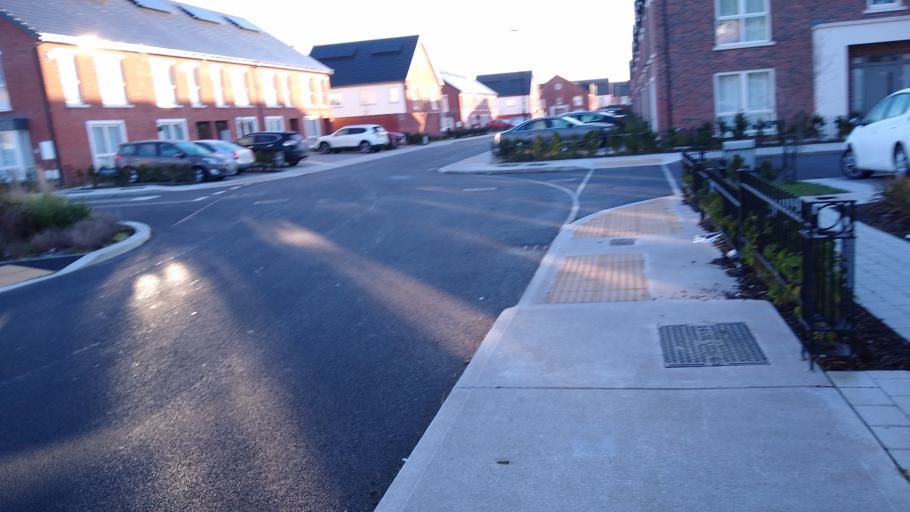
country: IE
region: Leinster
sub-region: An Mhi
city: Ashbourne
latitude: 53.5077
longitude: -6.4162
